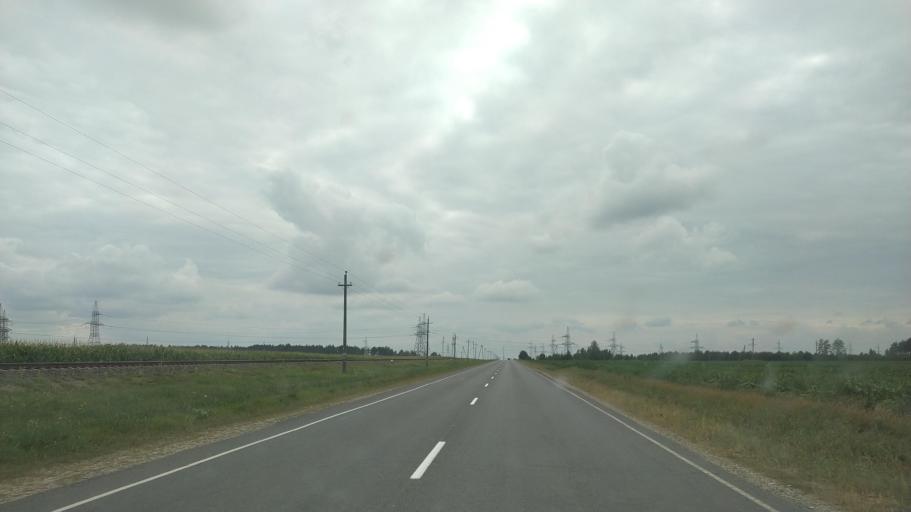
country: BY
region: Brest
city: Byelaazyorsk
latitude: 52.5203
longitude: 25.1507
